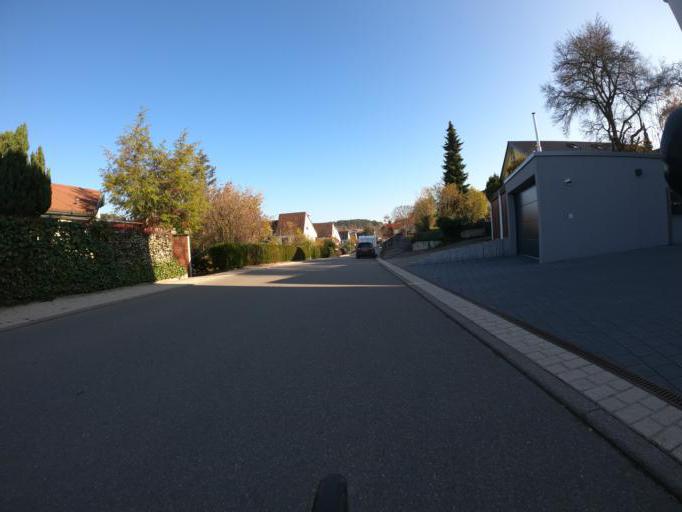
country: DE
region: Baden-Wuerttemberg
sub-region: Regierungsbezirk Stuttgart
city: Weil der Stadt
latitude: 48.7564
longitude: 8.8842
